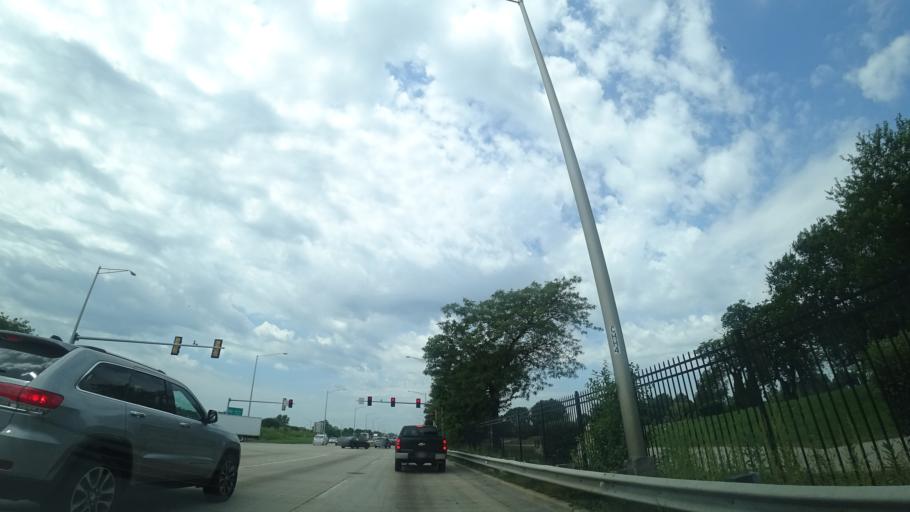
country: US
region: Illinois
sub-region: Cook County
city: Alsip
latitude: 41.6619
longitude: -87.7333
